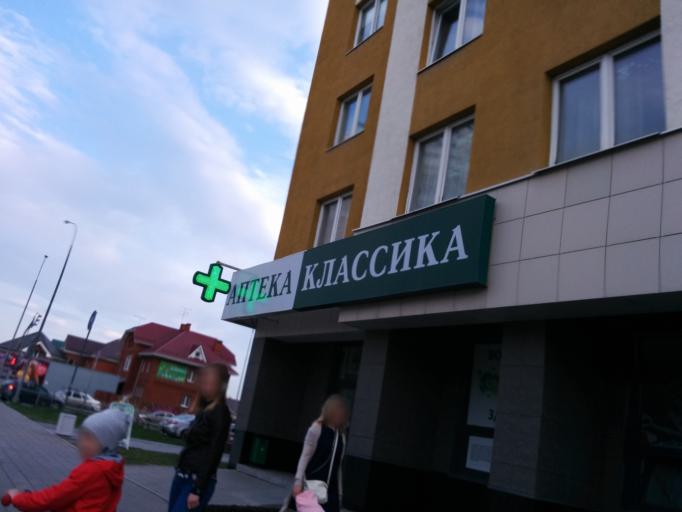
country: RU
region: Sverdlovsk
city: Sovkhoznyy
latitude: 56.7885
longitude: 60.5292
